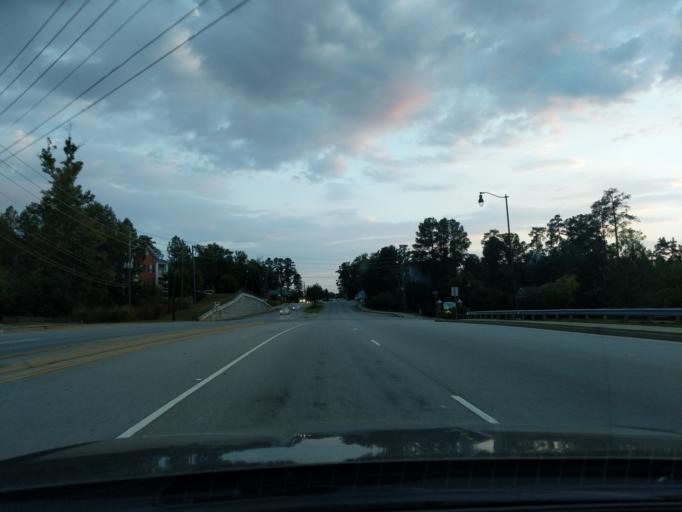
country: US
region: Georgia
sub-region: Columbia County
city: Martinez
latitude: 33.5171
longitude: -82.0248
